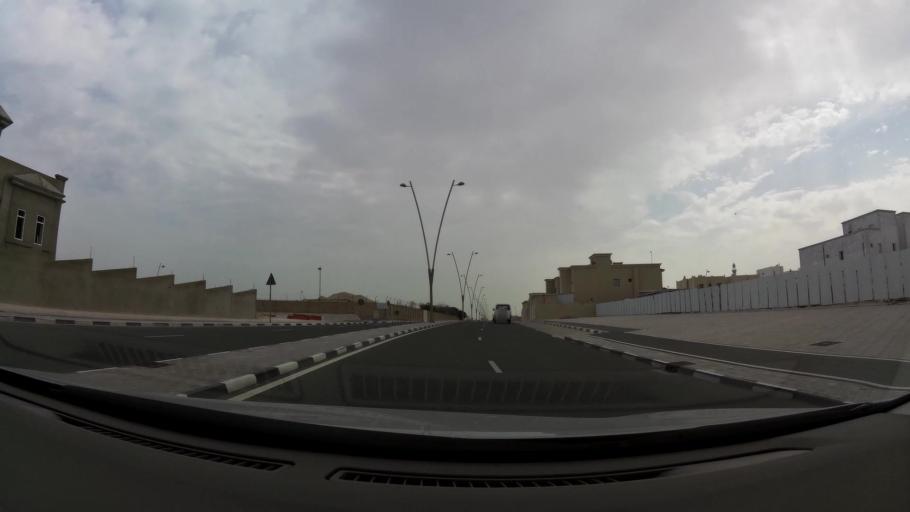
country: QA
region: Baladiyat ad Dawhah
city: Doha
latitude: 25.3415
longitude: 51.4945
